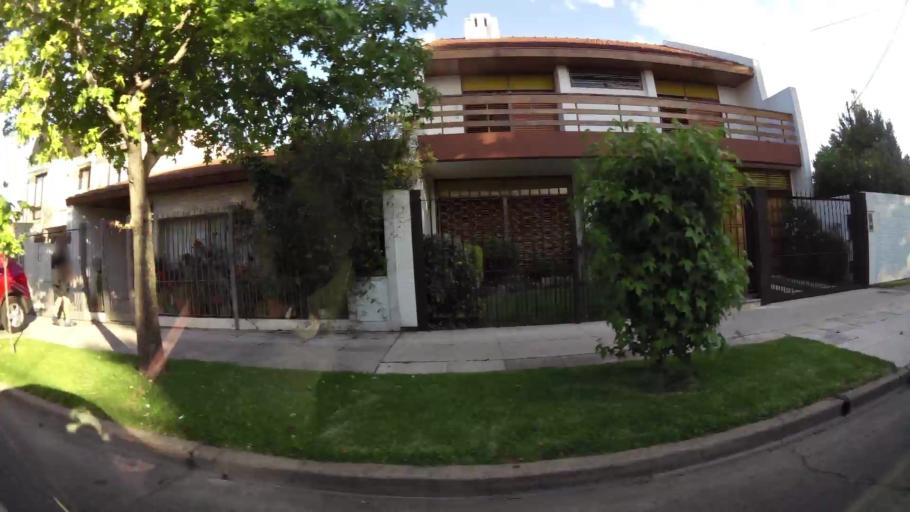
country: AR
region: Buenos Aires
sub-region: Partido de General San Martin
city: General San Martin
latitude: -34.5541
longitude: -58.5496
